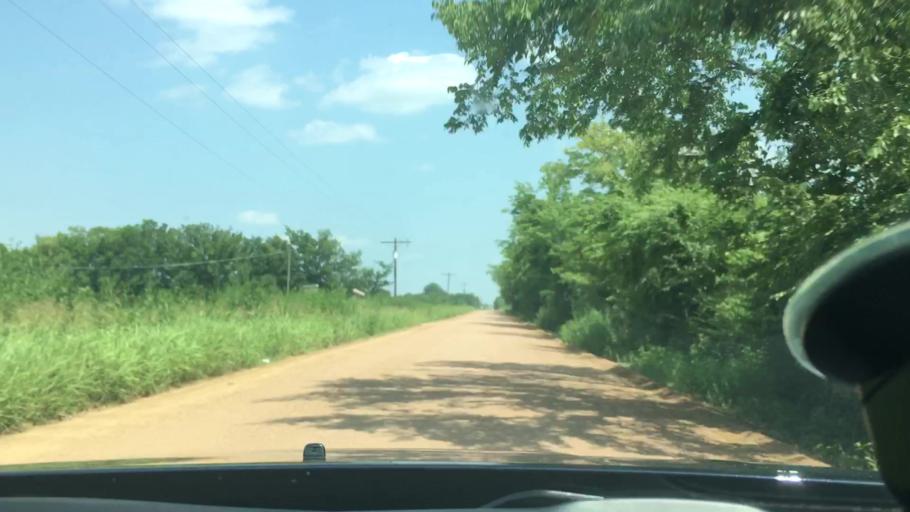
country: US
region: Oklahoma
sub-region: Johnston County
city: Tishomingo
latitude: 34.4196
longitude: -96.4867
